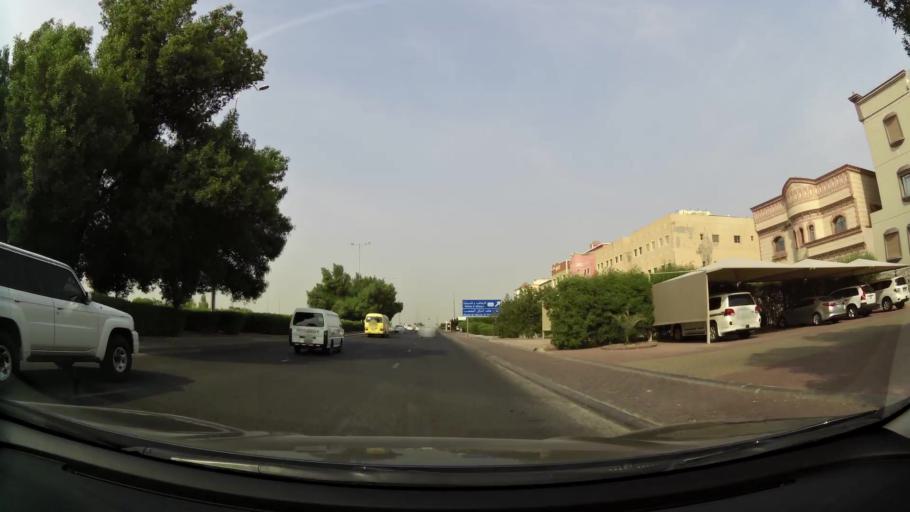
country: KW
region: Al Asimah
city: Ar Rabiyah
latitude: 29.2777
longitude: 47.9270
